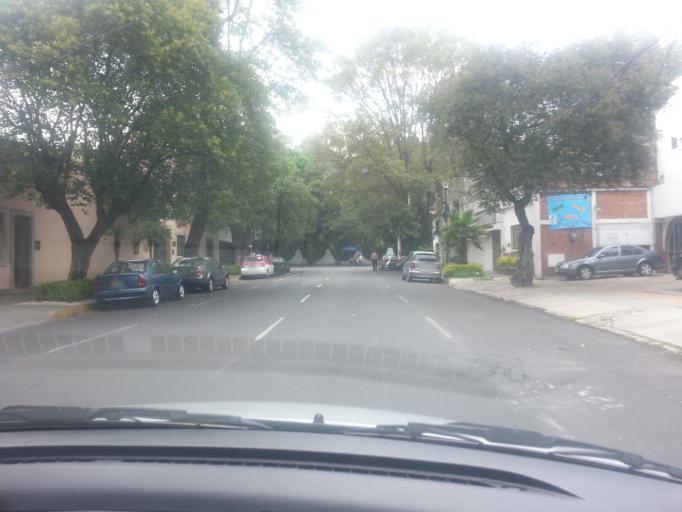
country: MX
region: Mexico City
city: Coyoacan
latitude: 19.3519
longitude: -99.1685
